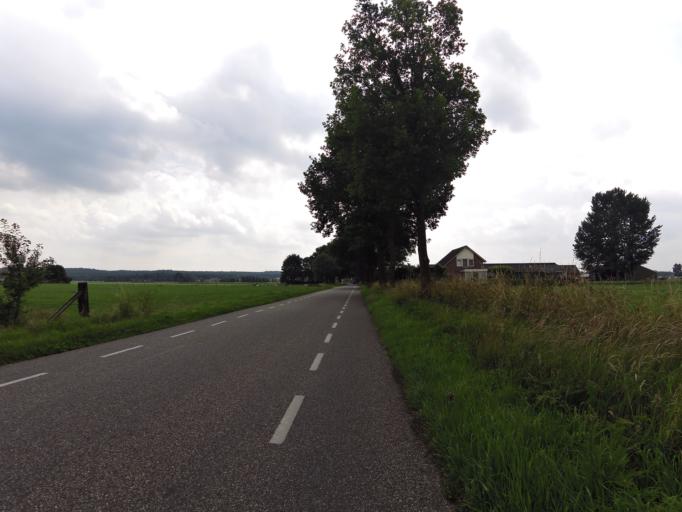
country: NL
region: Gelderland
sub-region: Gemeente Montferland
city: s-Heerenberg
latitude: 51.9348
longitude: 6.2037
